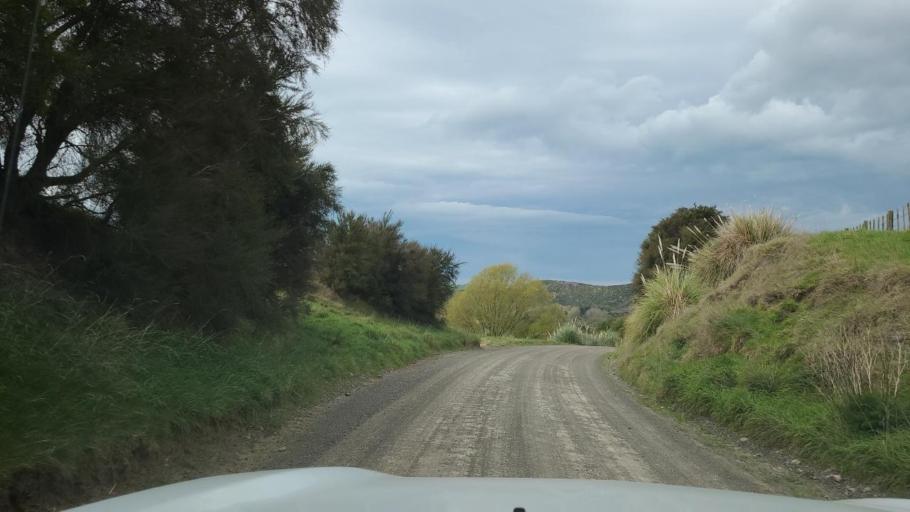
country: NZ
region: Hawke's Bay
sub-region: Napier City
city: Napier
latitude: -39.1788
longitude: 176.9595
